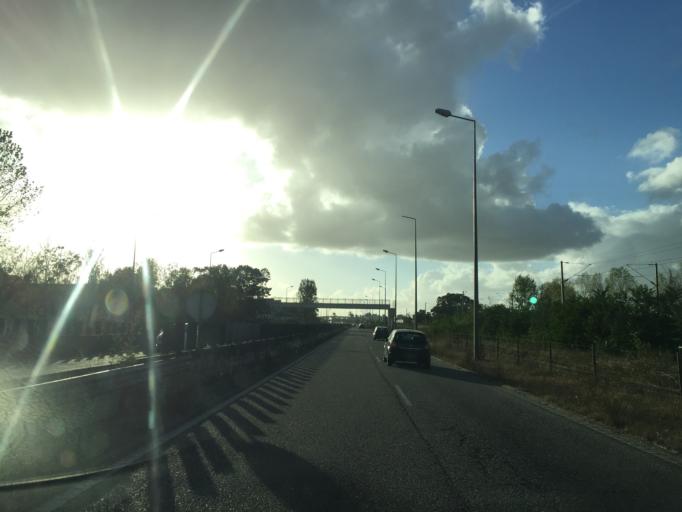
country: PT
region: Coimbra
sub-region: Coimbra
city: Coimbra
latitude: 40.2144
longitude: -8.4492
